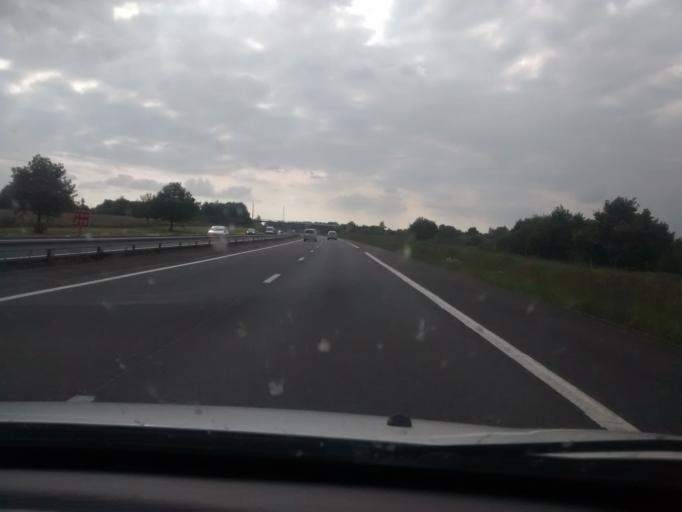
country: FR
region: Pays de la Loire
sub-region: Departement de la Mayenne
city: Vaiges
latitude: 48.0505
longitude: -0.4075
